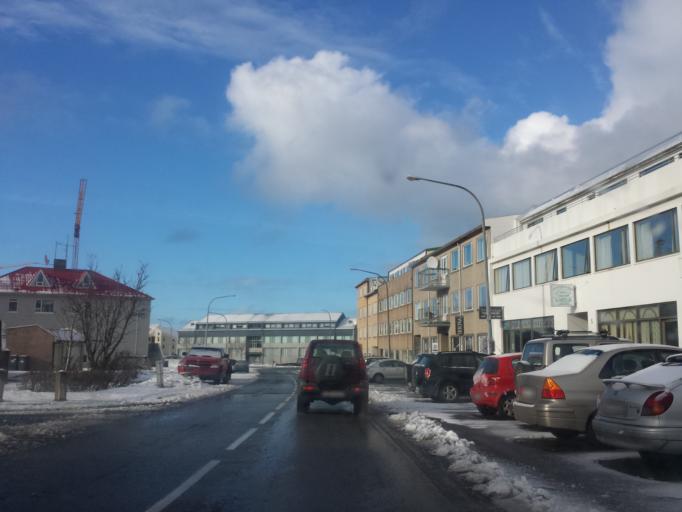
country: IS
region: Capital Region
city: Reykjavik
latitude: 64.1413
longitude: -21.9090
